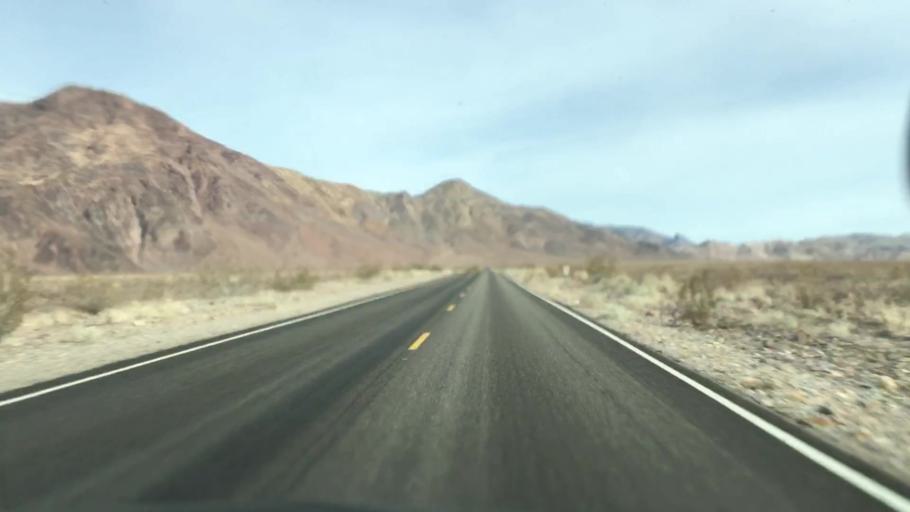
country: US
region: Nevada
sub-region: Nye County
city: Beatty
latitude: 36.6909
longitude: -117.0034
